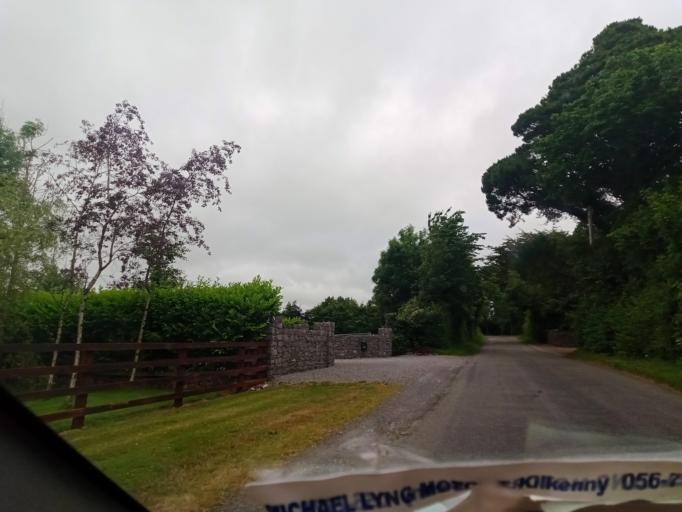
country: IE
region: Leinster
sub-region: Kilkenny
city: Ballyragget
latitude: 52.7410
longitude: -7.4168
